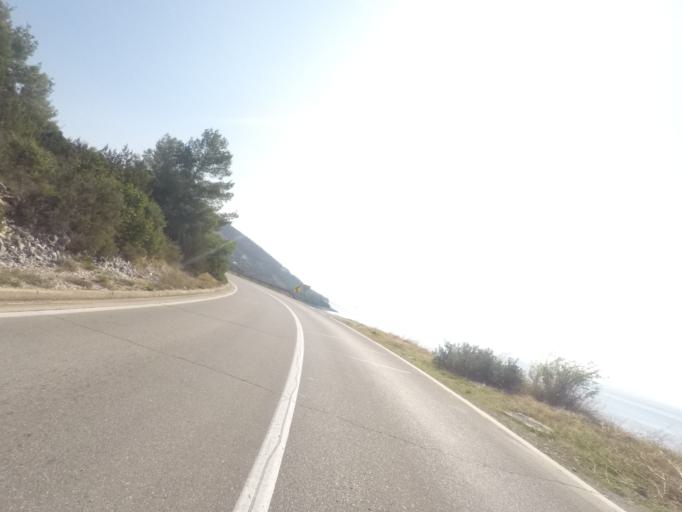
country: HR
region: Splitsko-Dalmatinska
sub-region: Grad Hvar
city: Hvar
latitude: 43.1610
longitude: 16.4899
